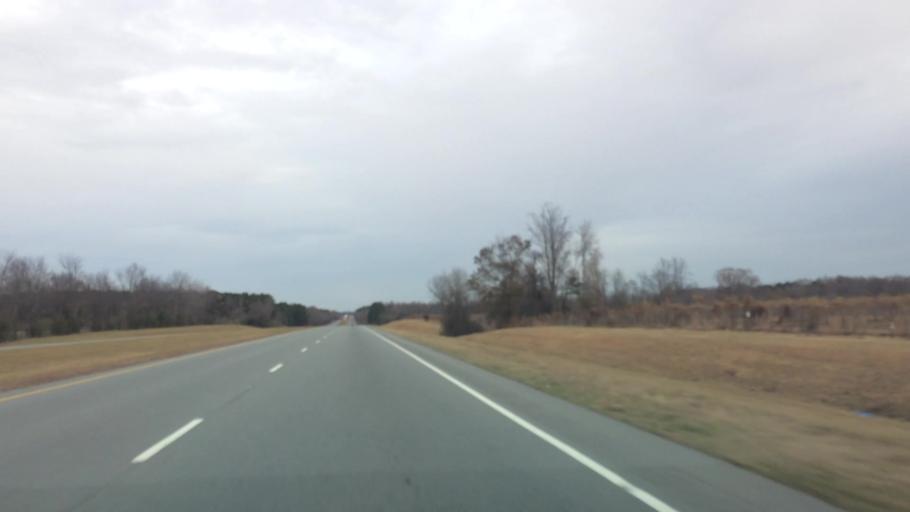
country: US
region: North Carolina
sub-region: Wayne County
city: Mount Olive
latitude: 35.1315
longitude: -78.1448
